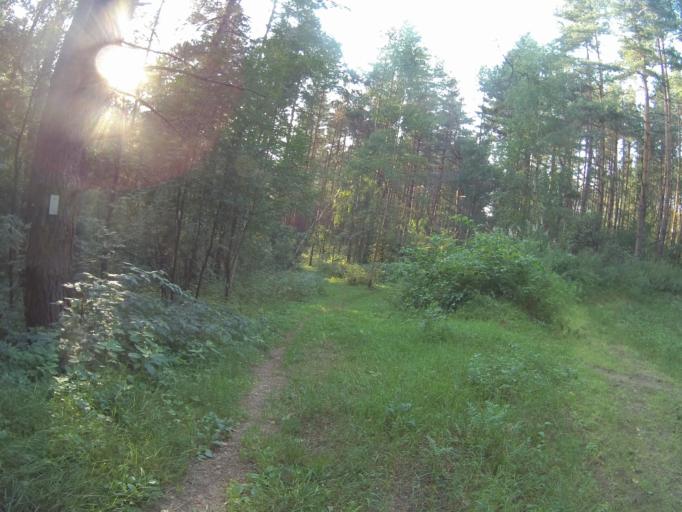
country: RU
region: Vladimir
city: Kommunar
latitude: 56.0693
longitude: 40.4371
